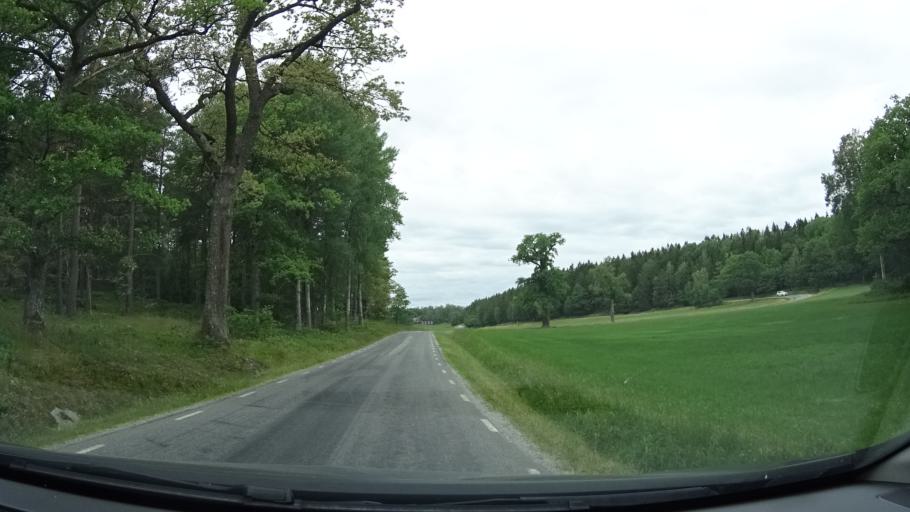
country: SE
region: Stockholm
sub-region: Varmdo Kommun
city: Hemmesta
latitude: 59.3628
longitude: 18.4751
